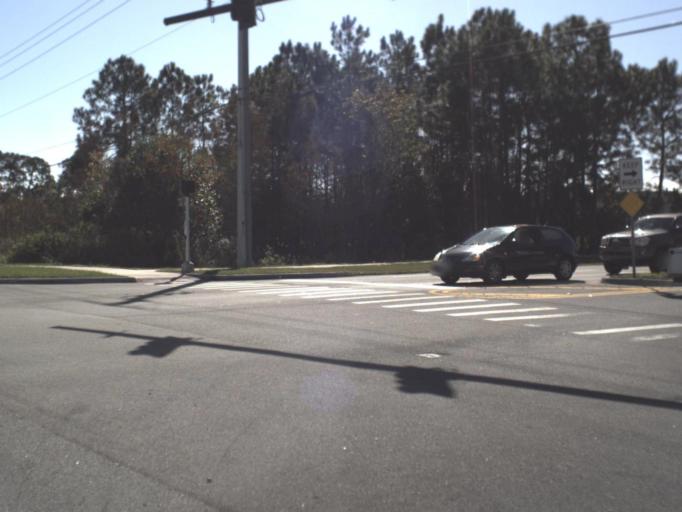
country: US
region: Florida
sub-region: Volusia County
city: Port Orange
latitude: 29.1084
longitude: -81.0354
